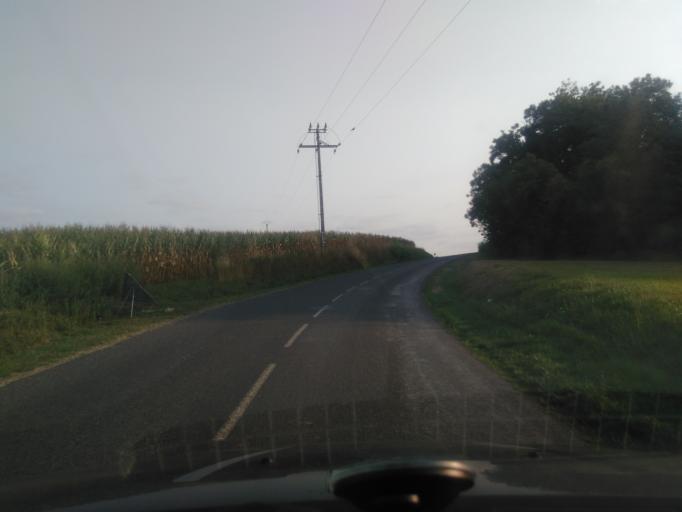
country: FR
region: Champagne-Ardenne
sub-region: Departement de la Marne
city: Fismes
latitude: 49.2651
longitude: 3.6978
